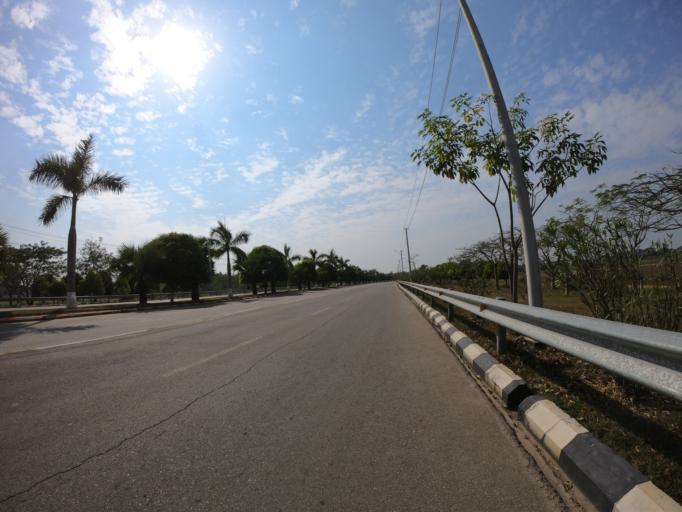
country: MM
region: Mandalay
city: Nay Pyi Taw
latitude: 19.6514
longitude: 96.1458
